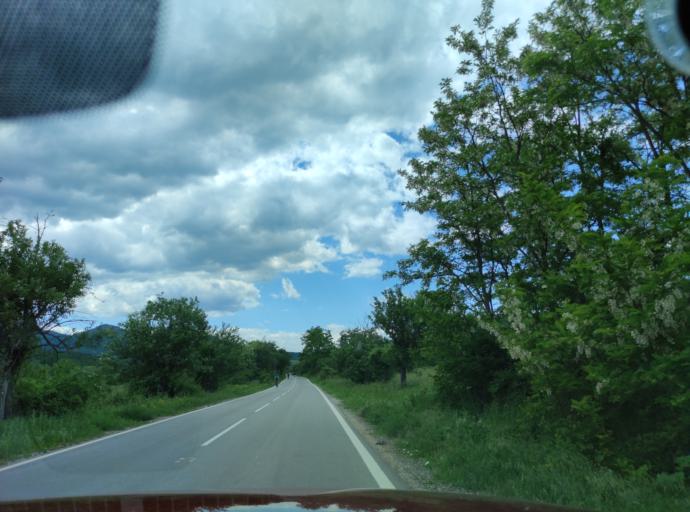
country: BG
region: Montana
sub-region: Obshtina Chiprovtsi
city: Chiprovtsi
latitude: 43.4466
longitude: 22.9209
